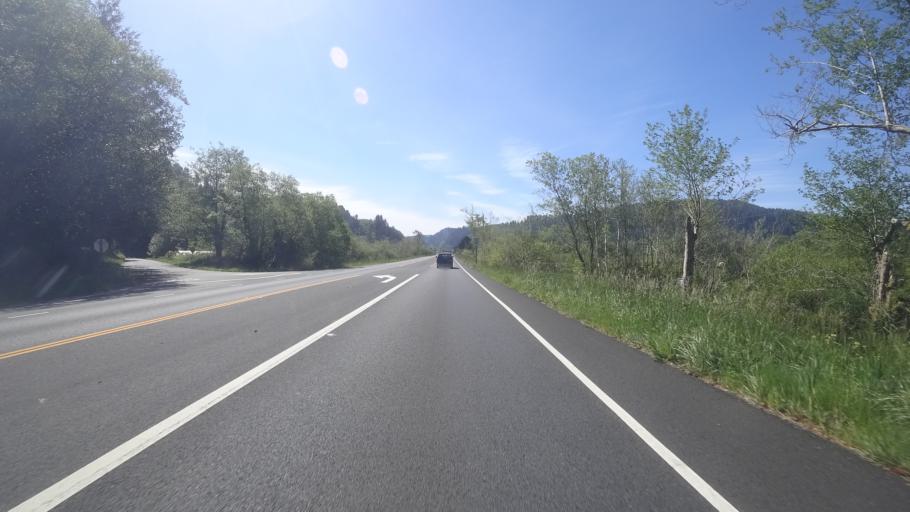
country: US
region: California
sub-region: Del Norte County
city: Bertsch-Oceanview
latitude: 41.5466
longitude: -124.0520
